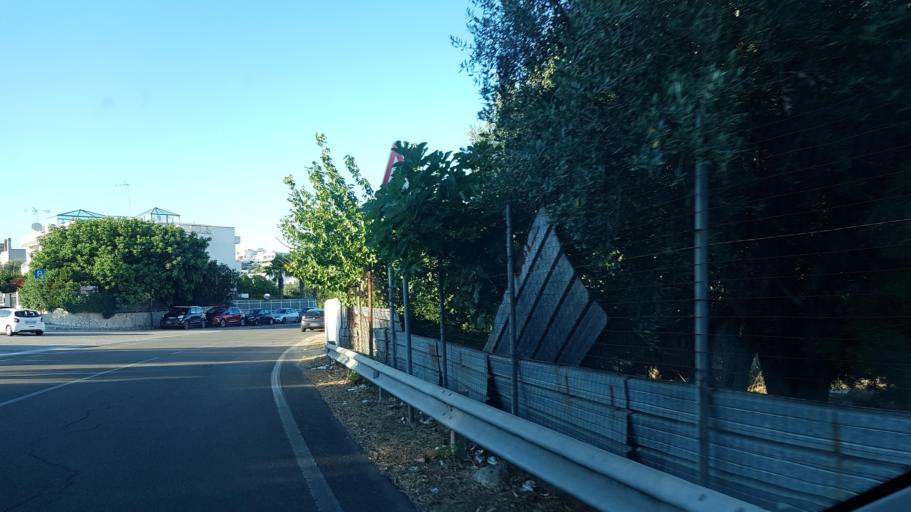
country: IT
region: Apulia
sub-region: Provincia di Lecce
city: Castro
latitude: 40.0020
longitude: 18.4215
